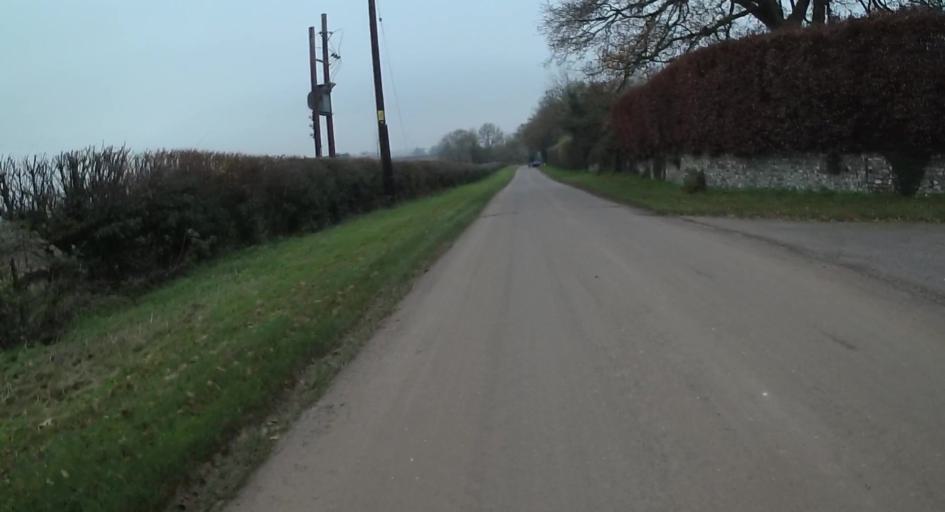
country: GB
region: England
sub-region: Hampshire
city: Kings Worthy
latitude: 51.1038
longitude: -1.2231
